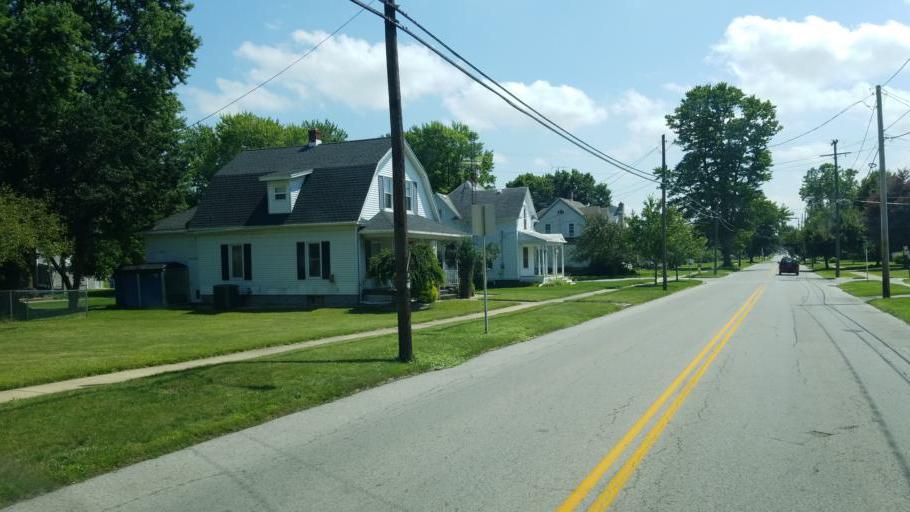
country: US
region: Ohio
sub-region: Huron County
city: Bellevue
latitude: 41.2821
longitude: -82.8384
